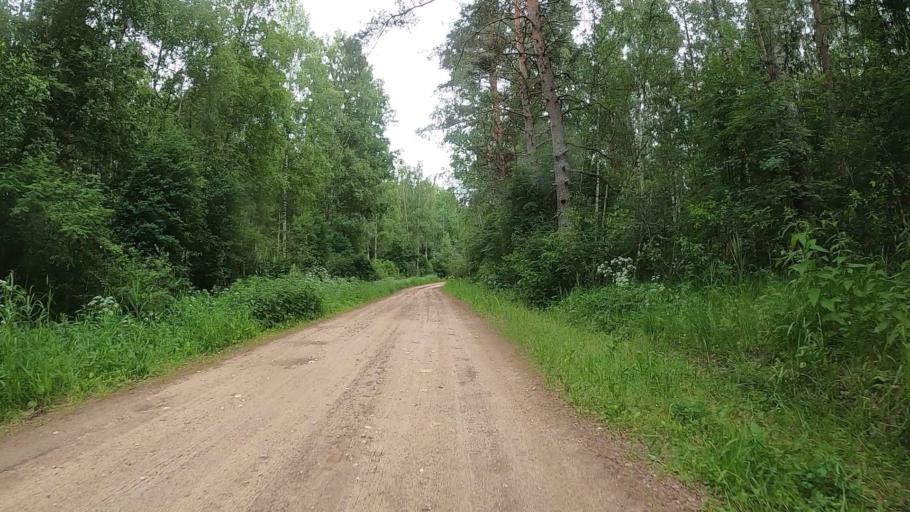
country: LV
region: Olaine
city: Olaine
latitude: 56.8319
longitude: 23.9309
